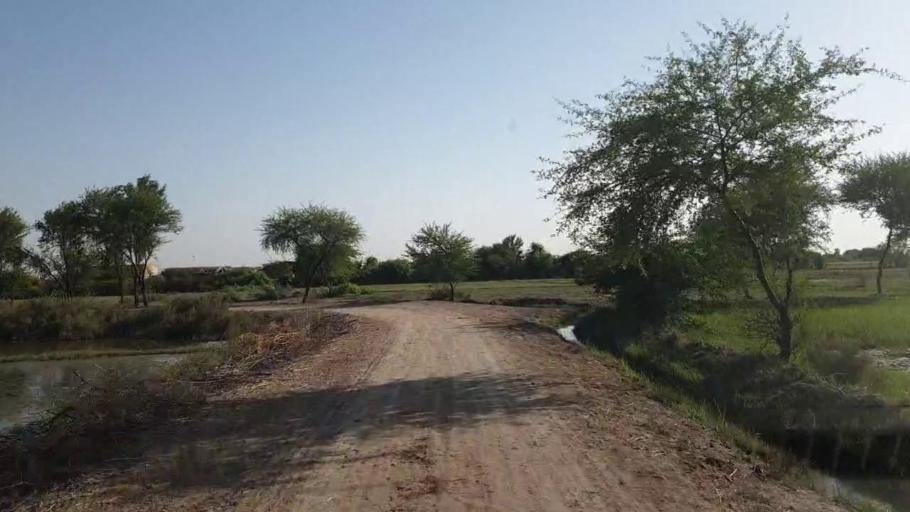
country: PK
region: Sindh
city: Badin
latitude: 24.5925
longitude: 68.9110
